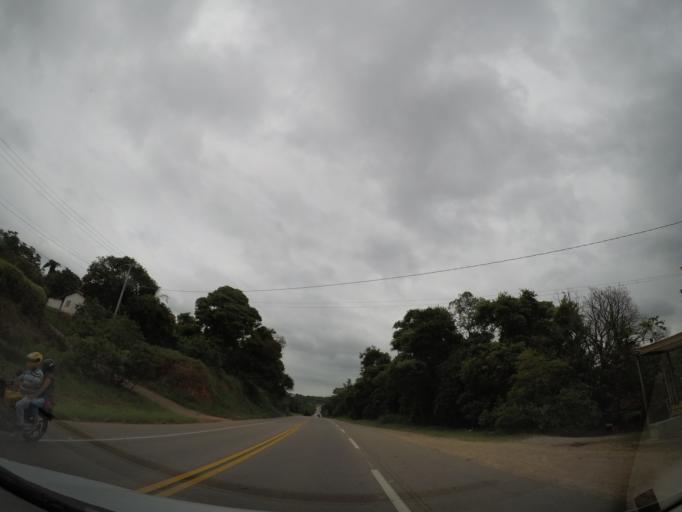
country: BR
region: Sao Paulo
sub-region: Louveira
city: Louveira
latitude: -23.0549
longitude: -46.9537
